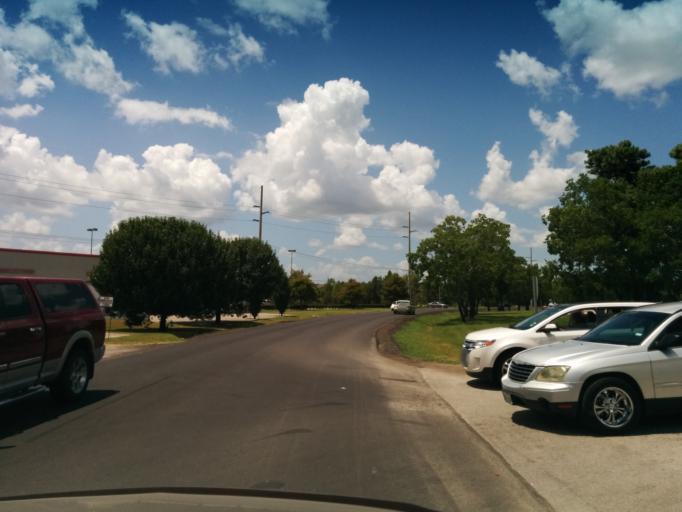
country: US
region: Texas
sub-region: Jefferson County
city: Beaumont
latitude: 30.1202
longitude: -94.1683
